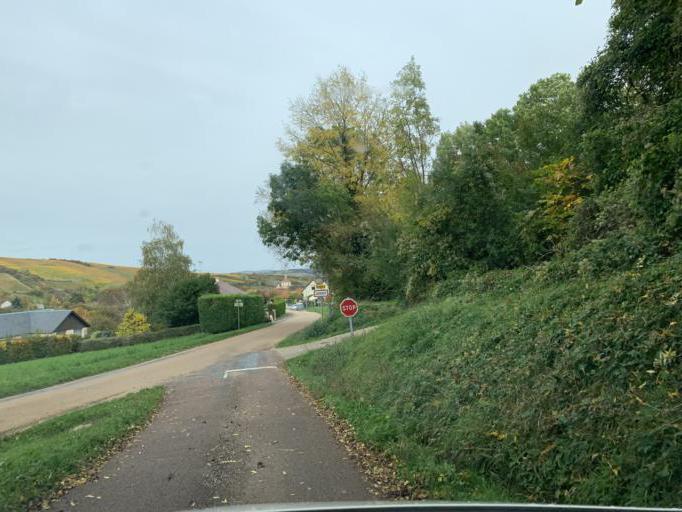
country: FR
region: Bourgogne
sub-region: Departement de l'Yonne
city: Champs-sur-Yonne
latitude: 47.7179
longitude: 3.5791
